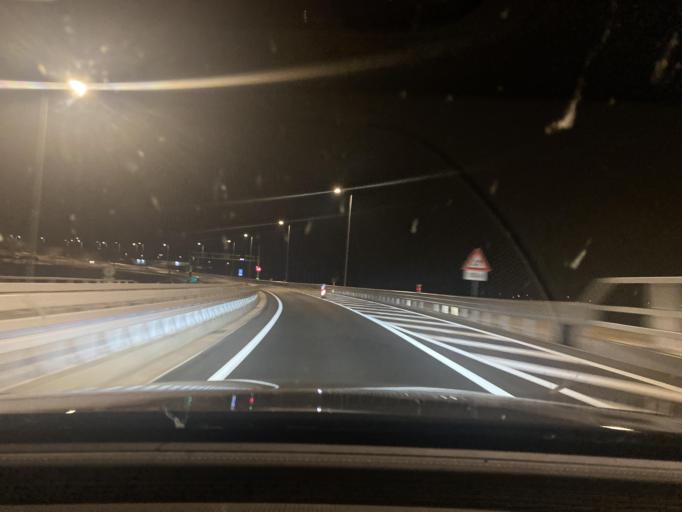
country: BA
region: Federation of Bosnia and Herzegovina
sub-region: Hercegovacko-Bosanski Kanton
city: Neum
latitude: 42.9228
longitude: 17.5274
